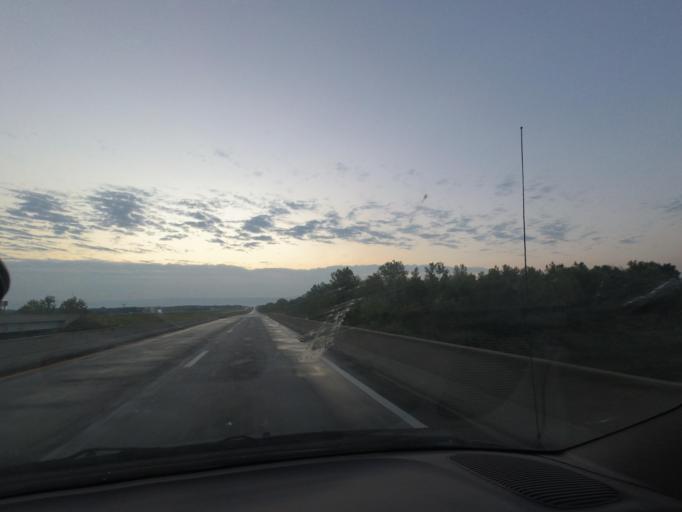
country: US
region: Missouri
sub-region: Macon County
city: Macon
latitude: 39.7601
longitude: -92.6921
